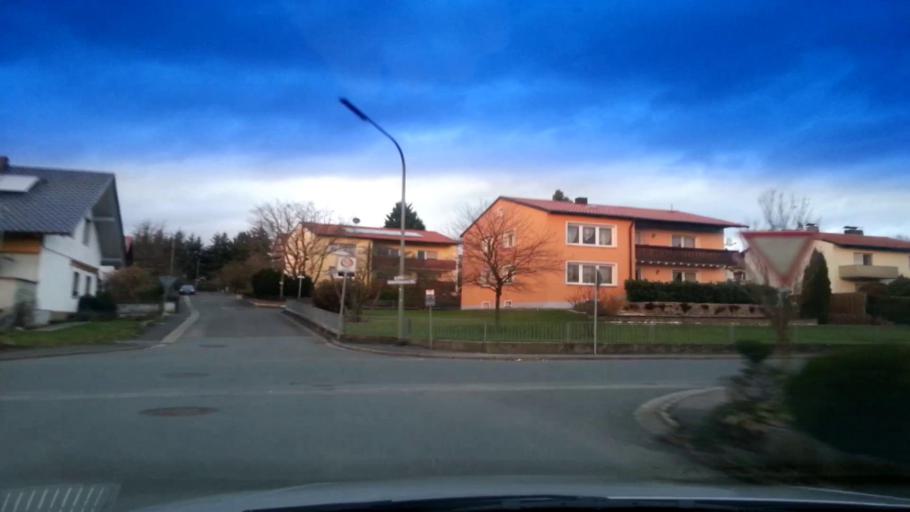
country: DE
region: Bavaria
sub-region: Upper Franconia
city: Schesslitz
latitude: 49.9744
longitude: 11.0417
